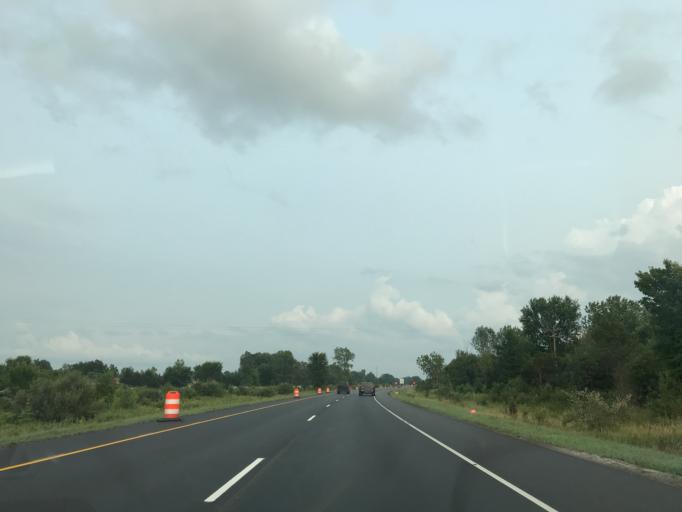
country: US
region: Michigan
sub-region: Livingston County
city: Fowlerville
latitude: 42.6463
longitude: -84.0534
